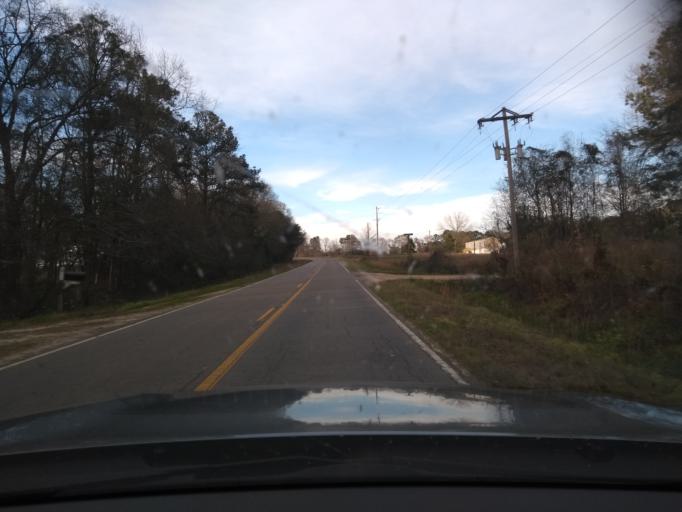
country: US
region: Georgia
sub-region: Evans County
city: Claxton
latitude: 32.2387
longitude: -81.7699
